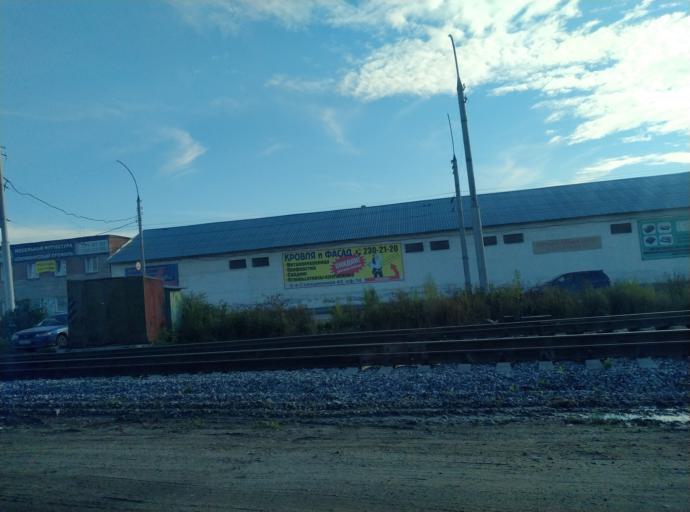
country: RU
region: Novosibirsk
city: Tolmachevo
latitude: 55.0132
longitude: 82.8105
